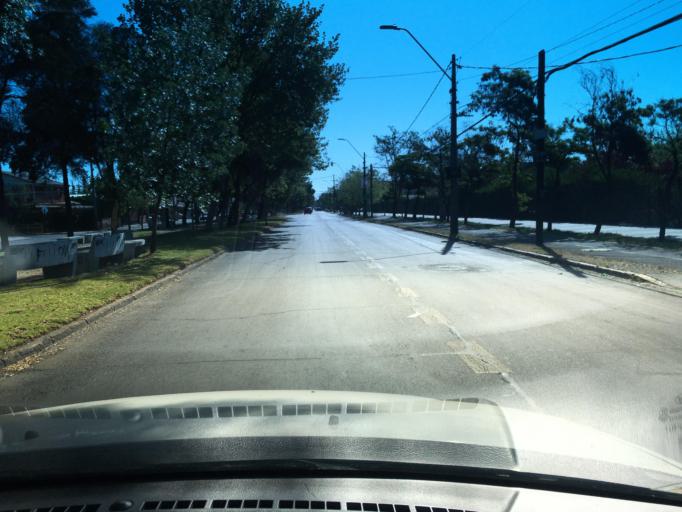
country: CL
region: Santiago Metropolitan
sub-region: Provincia de Santiago
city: Santiago
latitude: -33.5078
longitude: -70.6196
